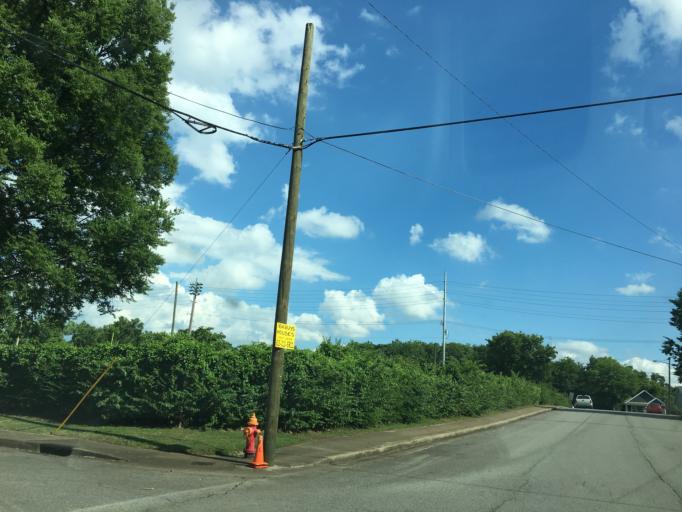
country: US
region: Tennessee
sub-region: Davidson County
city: Nashville
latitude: 36.1631
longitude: -86.8177
